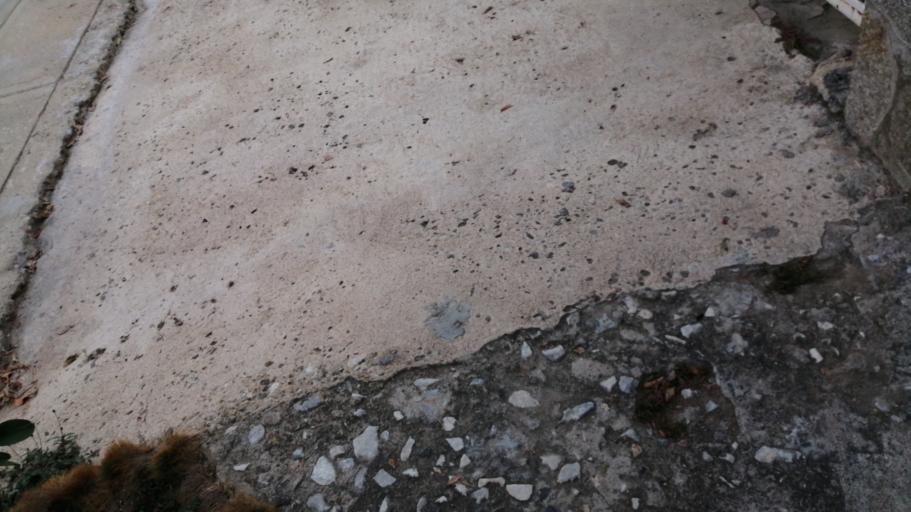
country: MX
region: Guerrero
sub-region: Acapulco de Juarez
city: Colonia Alborada
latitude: 16.8497
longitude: -99.8444
